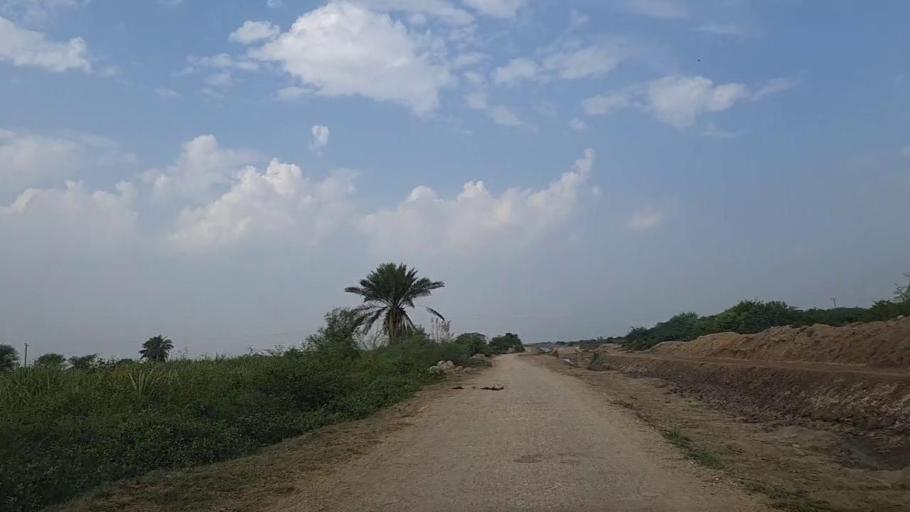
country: PK
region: Sindh
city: Daro Mehar
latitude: 24.7194
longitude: 68.1388
